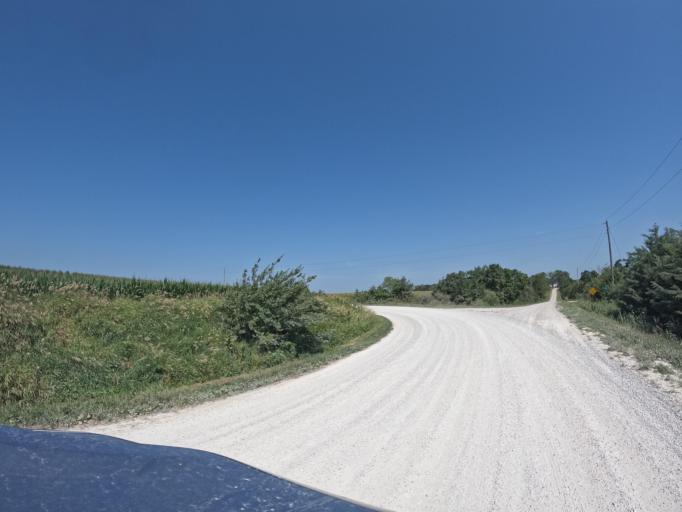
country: US
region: Iowa
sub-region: Henry County
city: Mount Pleasant
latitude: 40.8887
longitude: -91.5745
